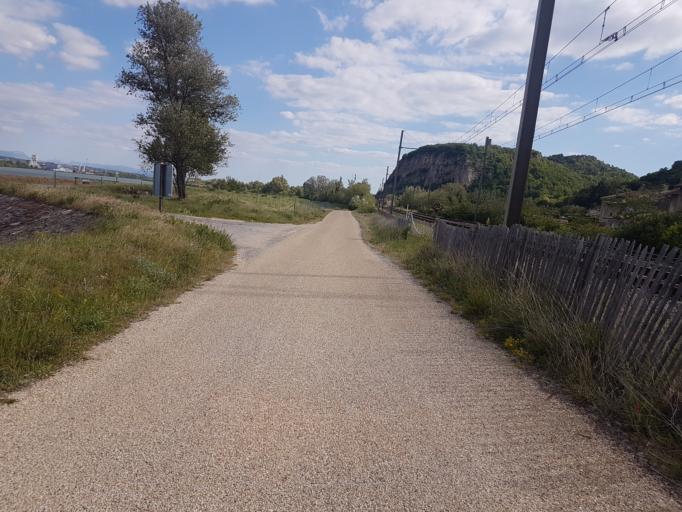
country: FR
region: Rhone-Alpes
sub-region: Departement de l'Ardeche
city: Soyons
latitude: 44.8947
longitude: 4.8518
